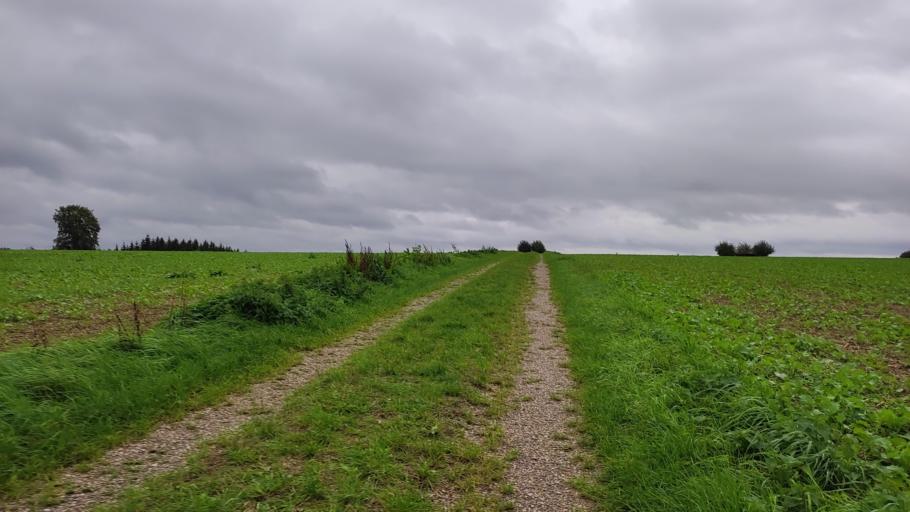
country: DE
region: Bavaria
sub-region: Swabia
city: Altenmunster
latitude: 48.4498
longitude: 10.6195
